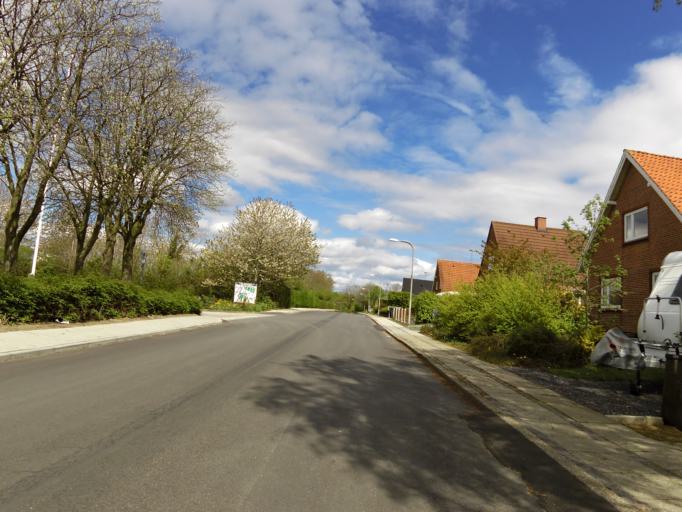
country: DK
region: South Denmark
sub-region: Haderslev Kommune
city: Gram
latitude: 55.2881
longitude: 9.0541
